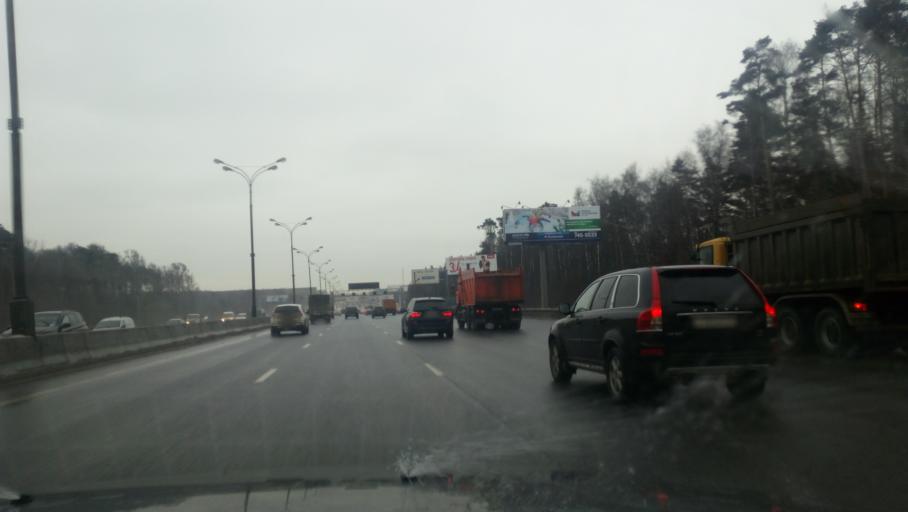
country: RU
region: Moskovskaya
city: Vostryakovo
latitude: 55.6488
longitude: 37.4479
